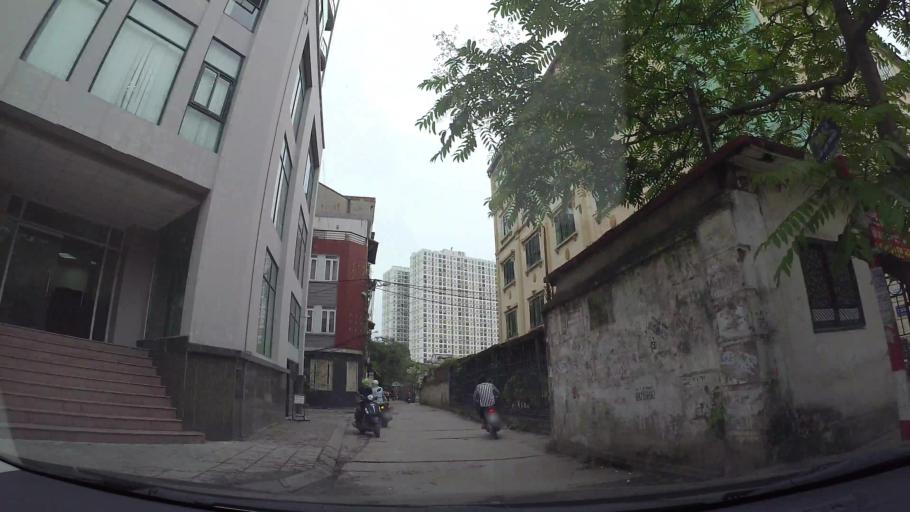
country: VN
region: Ha Noi
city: Hai BaTrung
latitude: 21.0011
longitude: 105.8669
